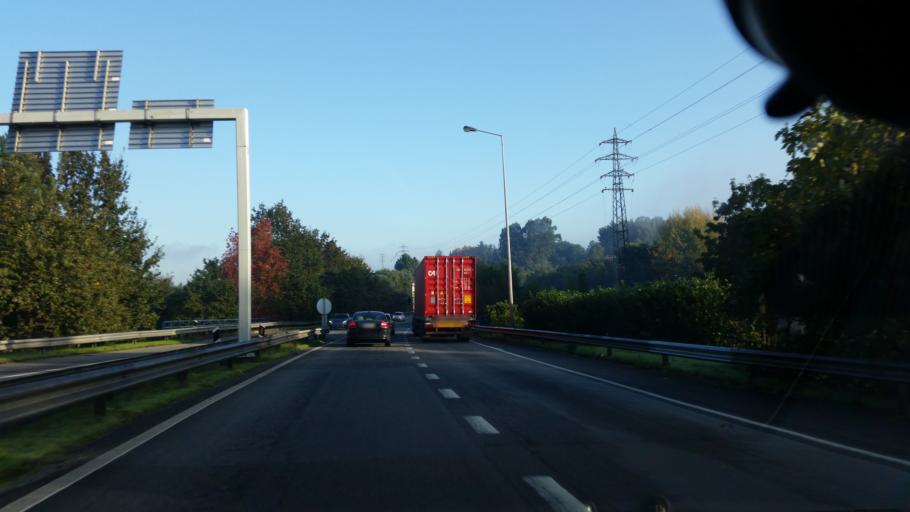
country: PT
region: Porto
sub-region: Santo Tirso
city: Sao Miguel do Couto
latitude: 41.3306
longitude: -8.4708
